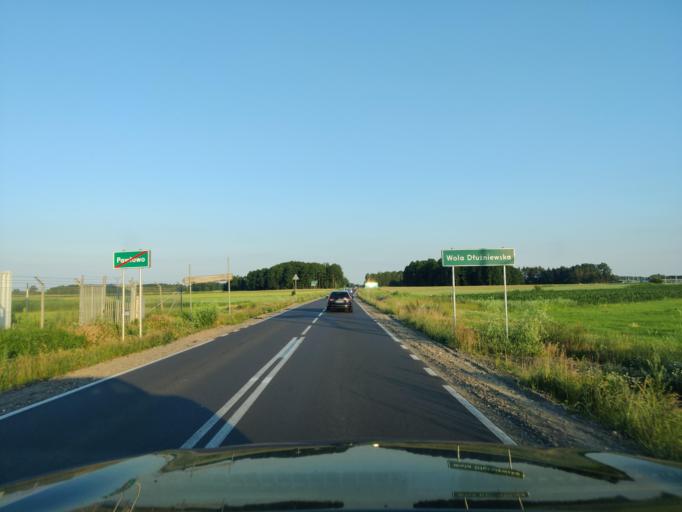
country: PL
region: Masovian Voivodeship
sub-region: Powiat plonski
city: Baboszewo
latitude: 52.7186
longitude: 20.3275
